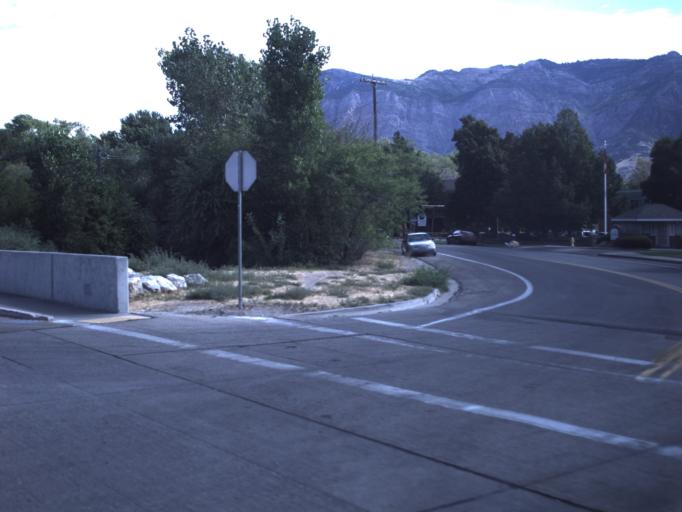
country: US
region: Utah
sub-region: Weber County
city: Ogden
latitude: 41.2335
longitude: -111.9701
